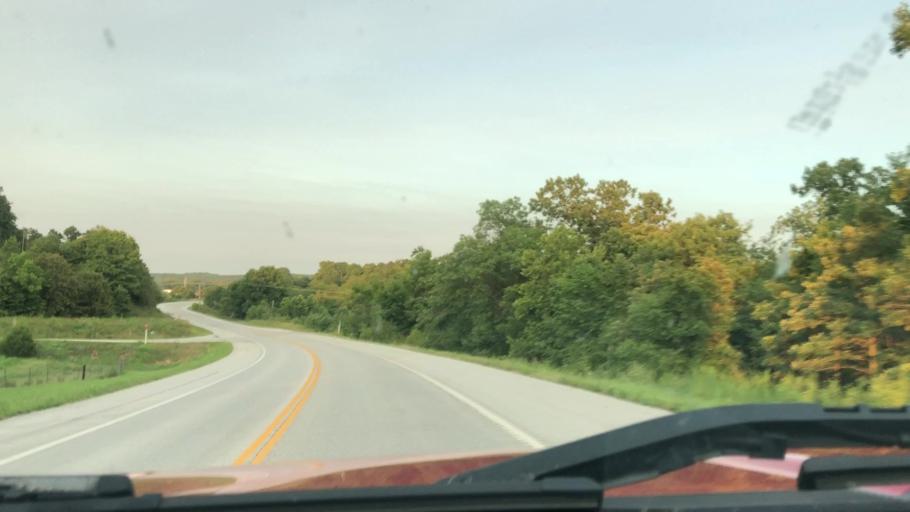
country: US
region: Missouri
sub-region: Jasper County
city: Duquesne
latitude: 36.9690
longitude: -94.4426
